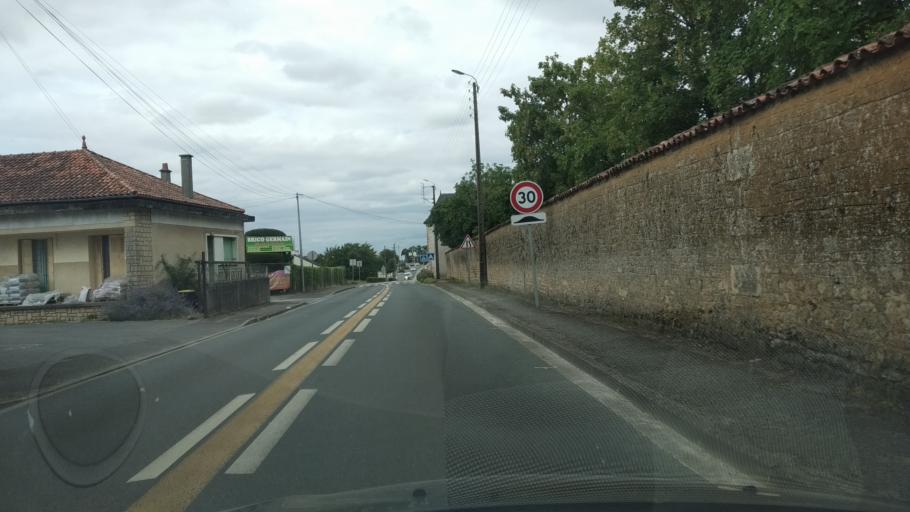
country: FR
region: Poitou-Charentes
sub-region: Departement de la Vienne
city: La Villedieu-du-Clain
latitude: 46.4581
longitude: 0.3671
